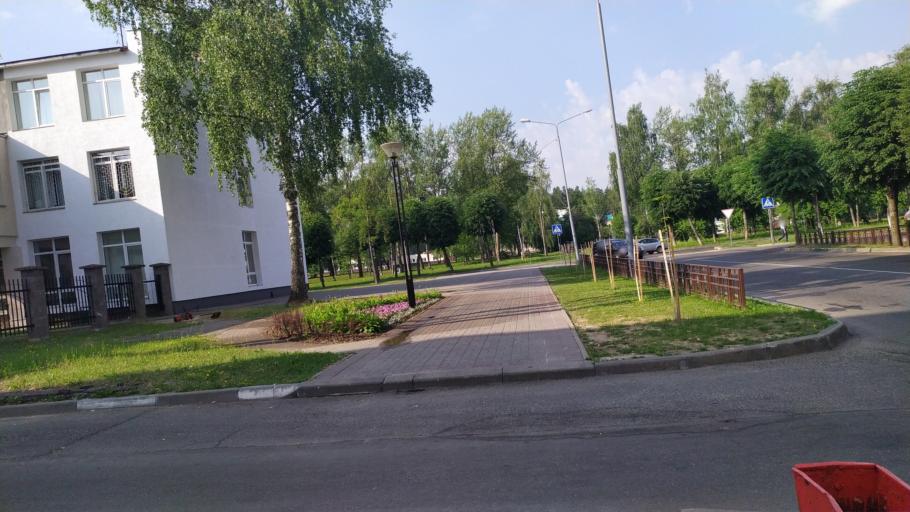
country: BY
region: Vitebsk
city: Navapolatsk
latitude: 55.5318
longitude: 28.6458
